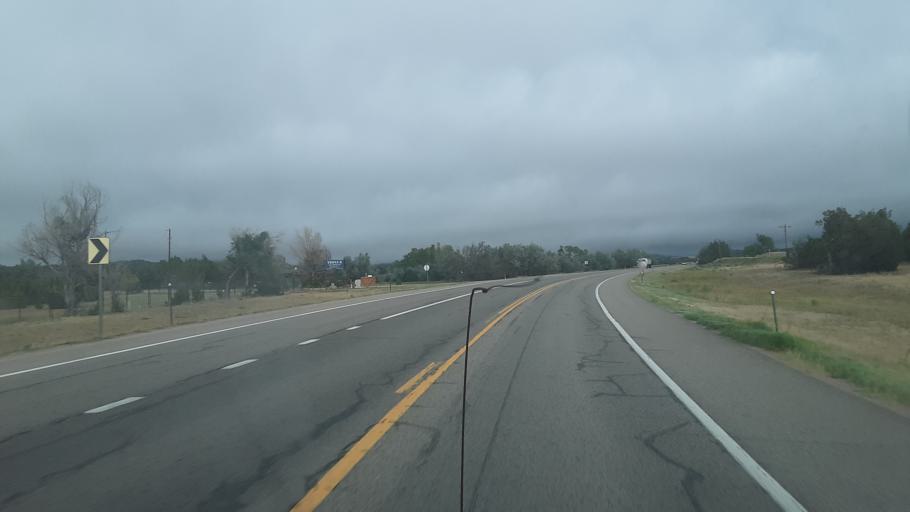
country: US
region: Colorado
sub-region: Huerfano County
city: Walsenburg
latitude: 37.5974
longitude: -104.8607
